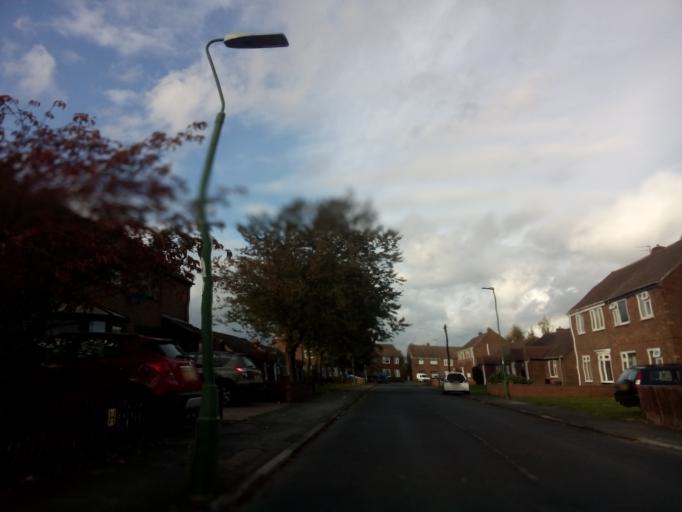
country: GB
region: England
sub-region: County Durham
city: Pittington
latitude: 54.7791
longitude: -1.5106
